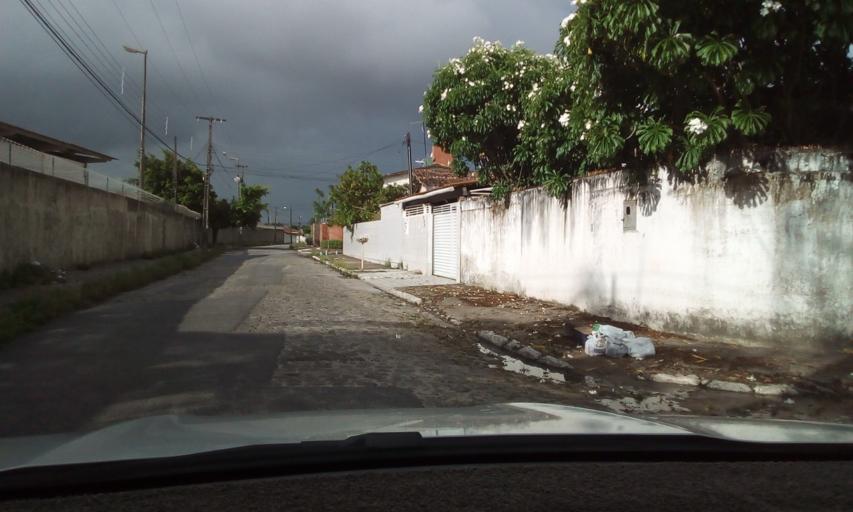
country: BR
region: Paraiba
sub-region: Joao Pessoa
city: Joao Pessoa
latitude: -7.1686
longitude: -34.8625
